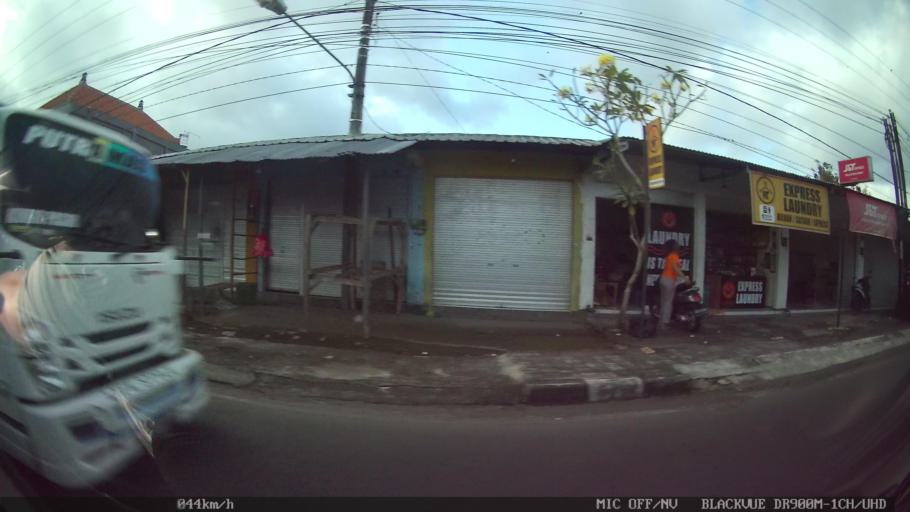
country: ID
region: Bali
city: Banjar Mambalkajanan
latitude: -8.5500
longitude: 115.2237
